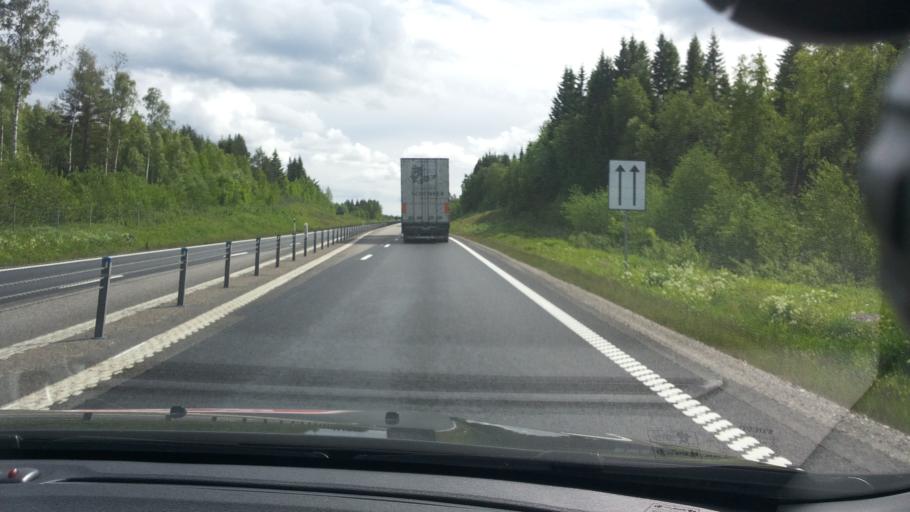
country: SE
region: Vaesternorrland
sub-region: Sundsvalls Kommun
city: Njurundabommen
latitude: 62.2216
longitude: 17.3719
